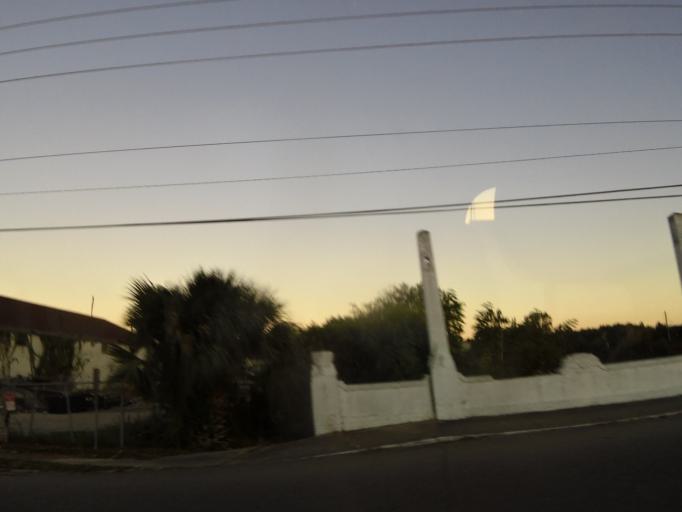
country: US
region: Florida
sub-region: Duval County
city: Jacksonville
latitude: 30.3333
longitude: -81.6522
